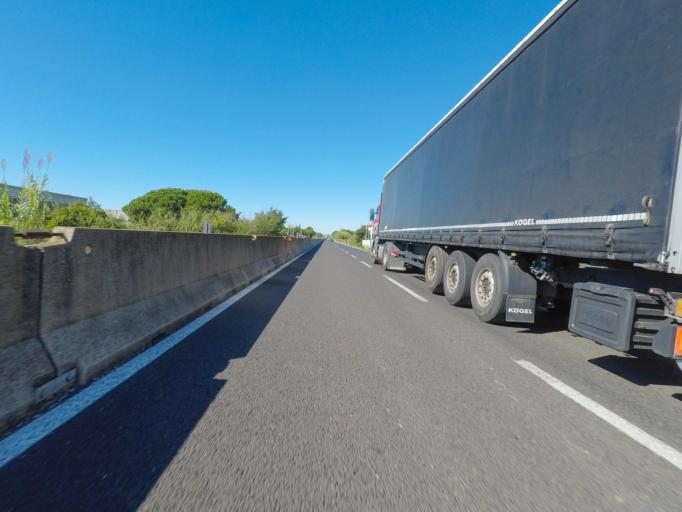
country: IT
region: Tuscany
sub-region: Provincia di Grosseto
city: Orbetello Scalo
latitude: 42.4649
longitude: 11.2418
